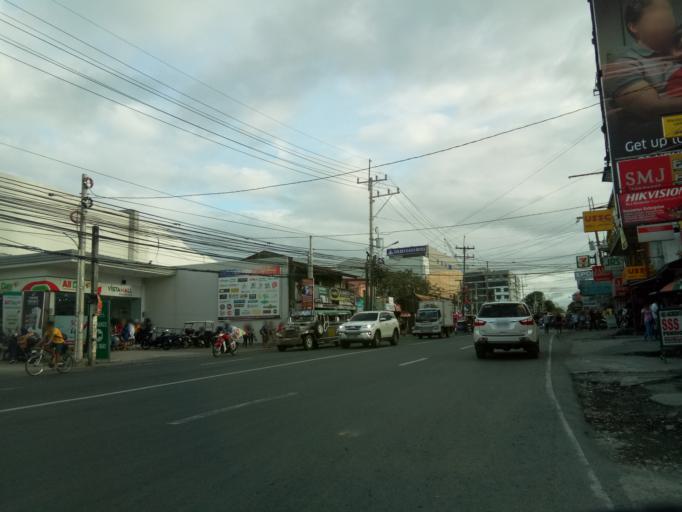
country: PH
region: Calabarzon
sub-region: Province of Cavite
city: Imus
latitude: 14.3858
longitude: 120.9778
